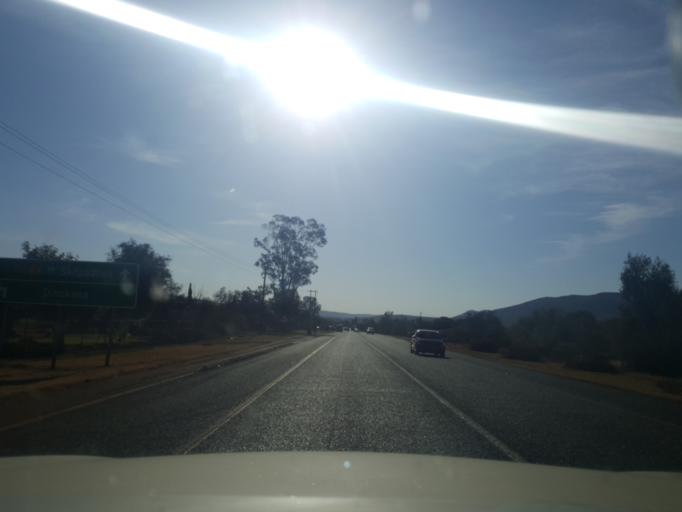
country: ZA
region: North-West
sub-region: Ngaka Modiri Molema District Municipality
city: Zeerust
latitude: -25.4527
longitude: 25.8713
